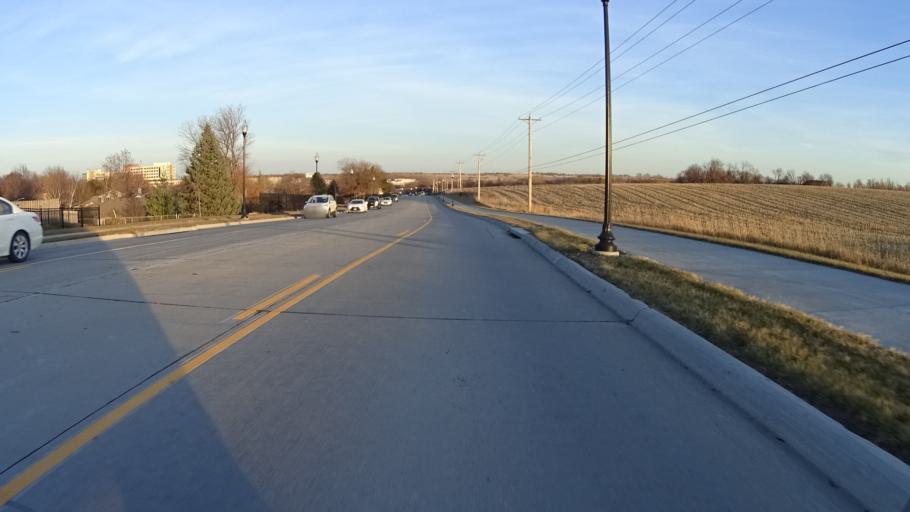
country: US
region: Nebraska
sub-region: Sarpy County
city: Papillion
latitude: 41.1326
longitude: -96.0484
